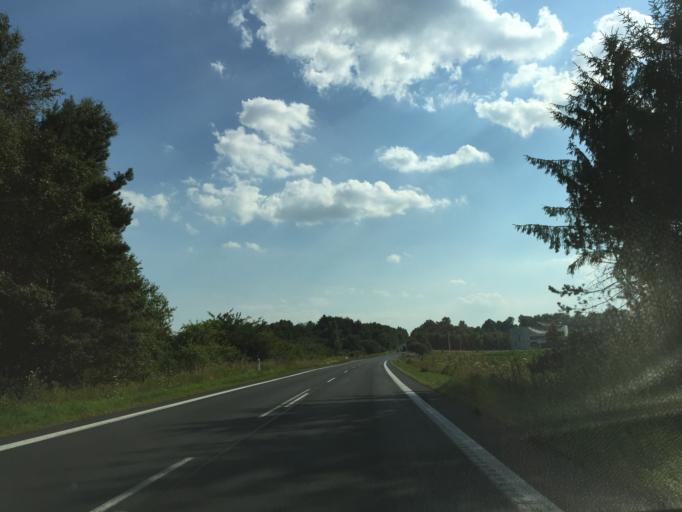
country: DK
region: Central Jutland
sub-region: Viborg Kommune
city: Bjerringbro
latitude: 56.3683
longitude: 9.6768
